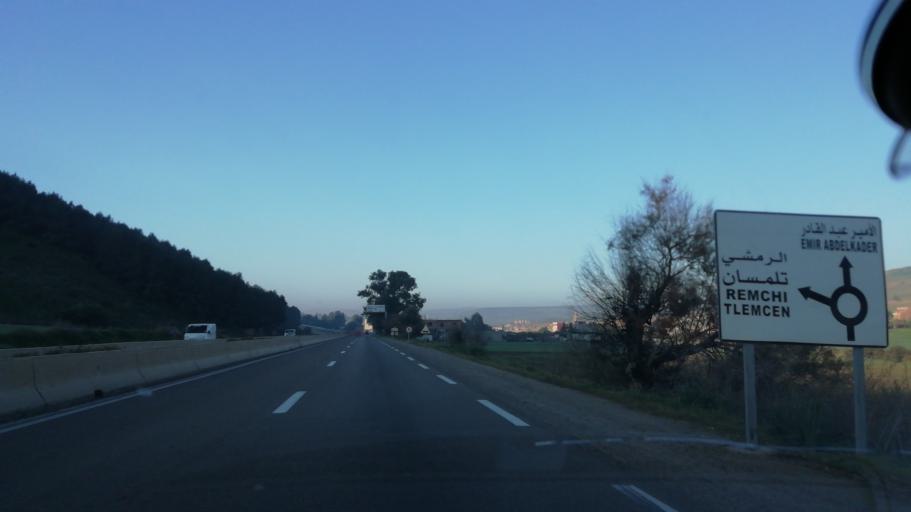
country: DZ
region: Ain Temouchent
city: Beni Saf
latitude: 35.2270
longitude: -1.3912
